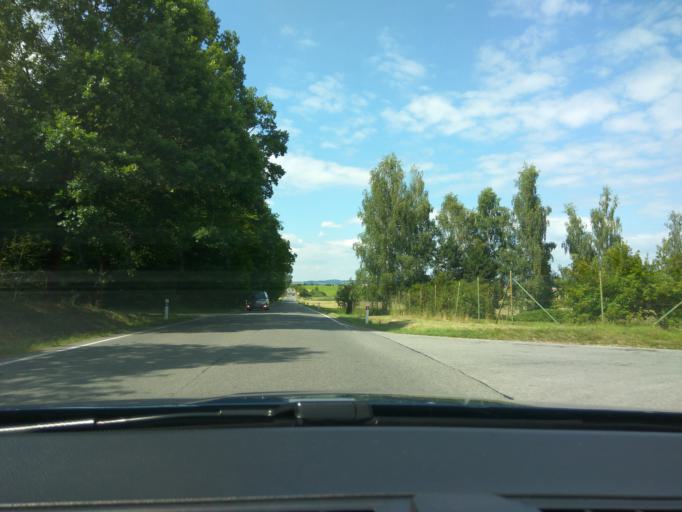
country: CZ
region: Jihocesky
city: Milevsko
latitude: 49.4260
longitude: 14.3592
